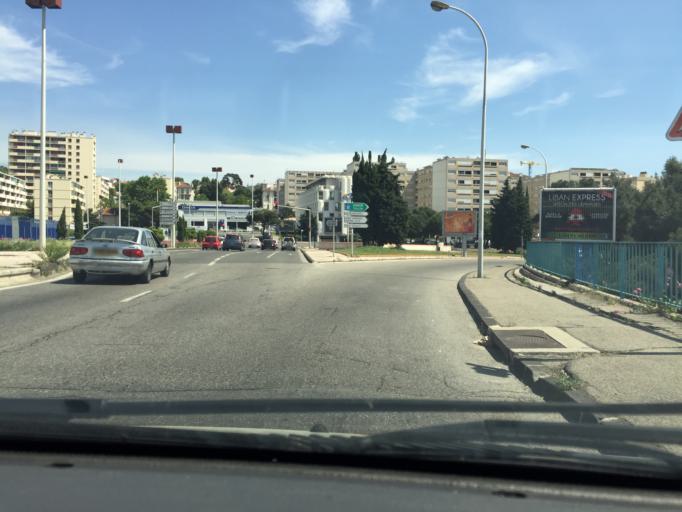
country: FR
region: Provence-Alpes-Cote d'Azur
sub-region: Departement des Bouches-du-Rhone
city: Marseille 13
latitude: 43.3143
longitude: 5.4046
